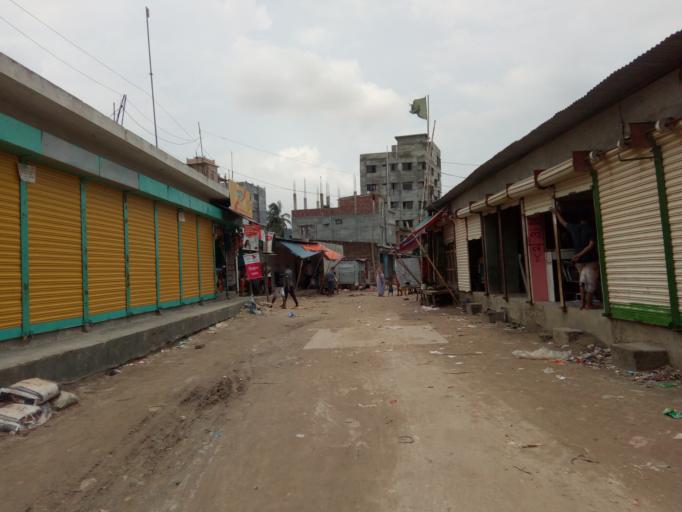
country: BD
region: Dhaka
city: Azimpur
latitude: 23.7280
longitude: 90.3697
